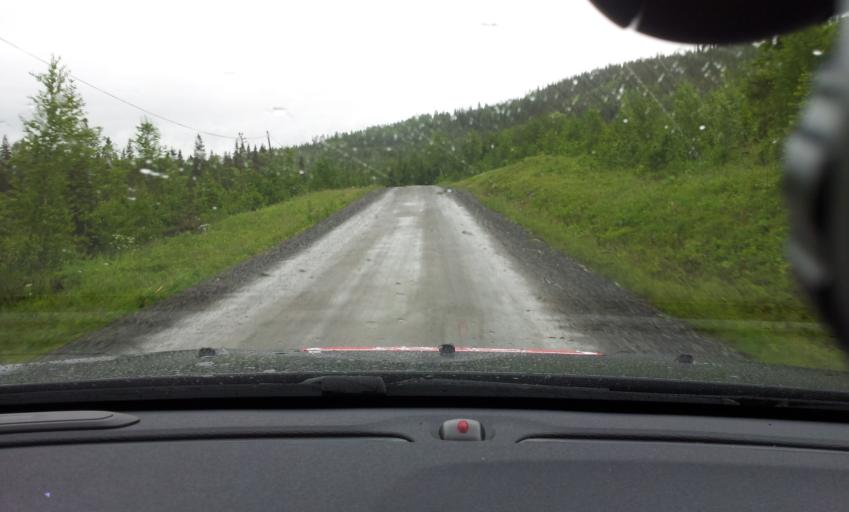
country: SE
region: Jaemtland
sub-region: Are Kommun
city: Are
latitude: 63.4923
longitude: 12.7675
